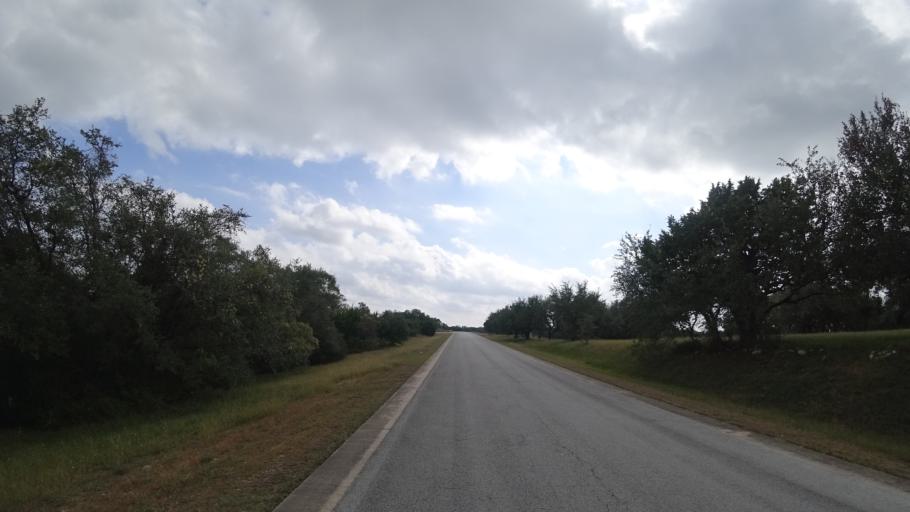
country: US
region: Texas
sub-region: Travis County
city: Barton Creek
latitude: 30.3049
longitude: -97.8921
